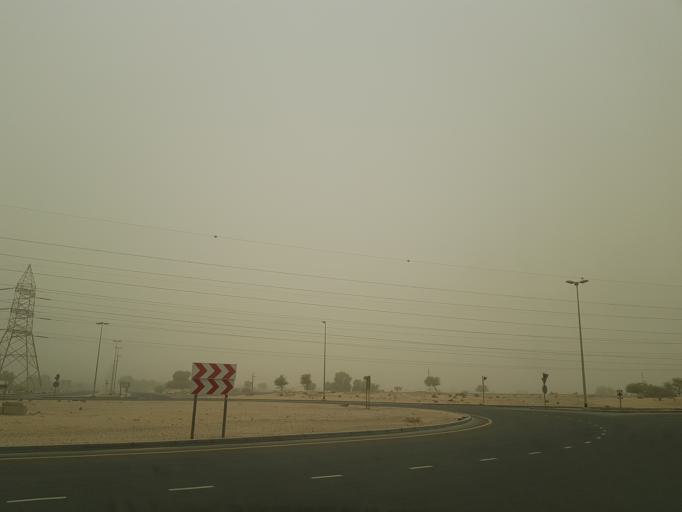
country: AE
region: Dubai
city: Dubai
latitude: 25.1408
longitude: 55.2890
